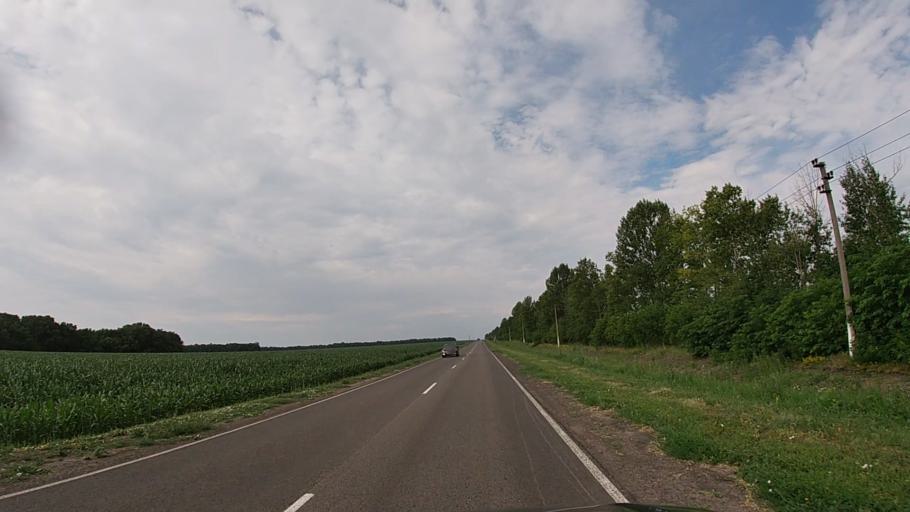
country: RU
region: Belgorod
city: Krasnaya Yaruga
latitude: 50.8279
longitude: 35.4733
